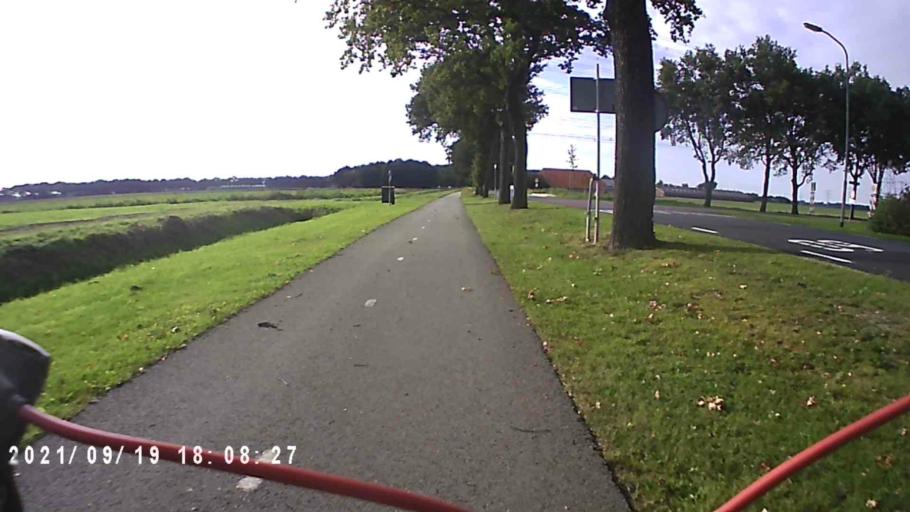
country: NL
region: Groningen
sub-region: Gemeente Delfzijl
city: Delfzijl
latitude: 53.2444
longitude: 6.8996
